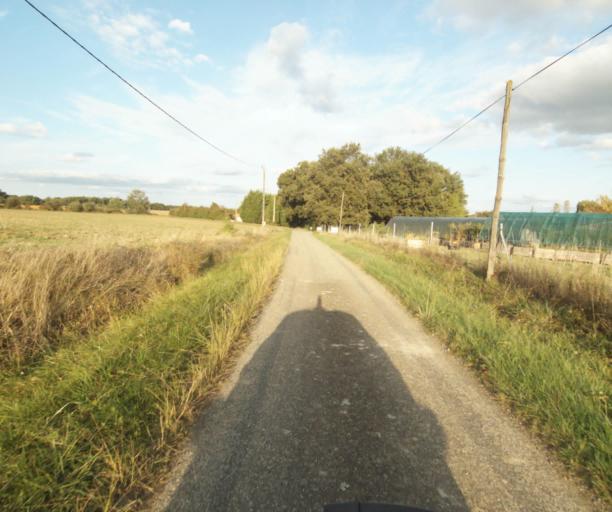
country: FR
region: Midi-Pyrenees
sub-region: Departement de la Haute-Garonne
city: Launac
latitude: 43.8291
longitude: 1.1273
